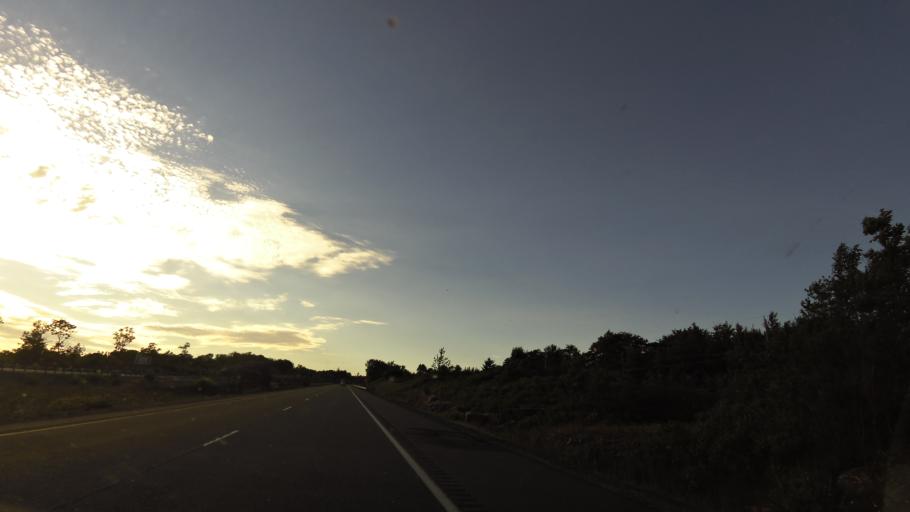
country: CA
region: Ontario
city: Midland
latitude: 44.8848
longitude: -79.7511
